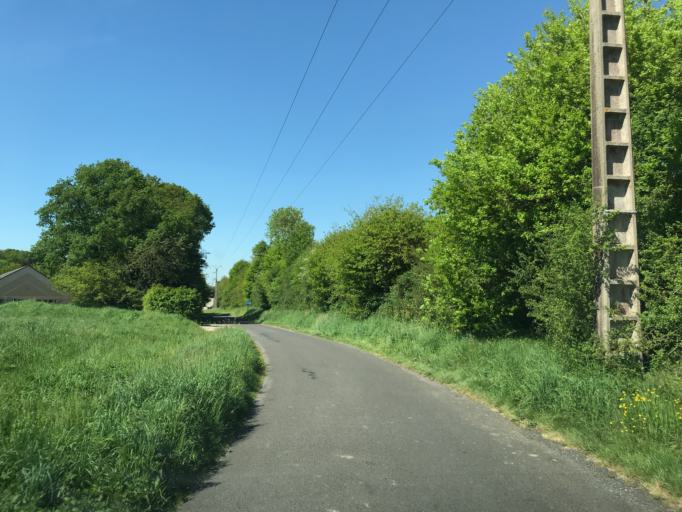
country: FR
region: Haute-Normandie
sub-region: Departement de l'Eure
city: Verneuil-sur-Avre
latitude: 48.7477
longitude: 0.9732
